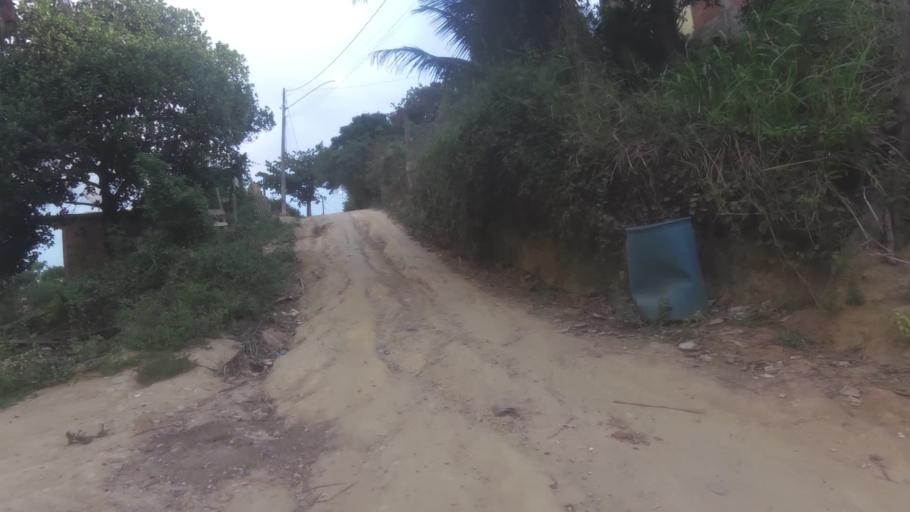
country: BR
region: Espirito Santo
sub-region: Itapemirim
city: Itapemirim
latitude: -21.0199
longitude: -40.8197
